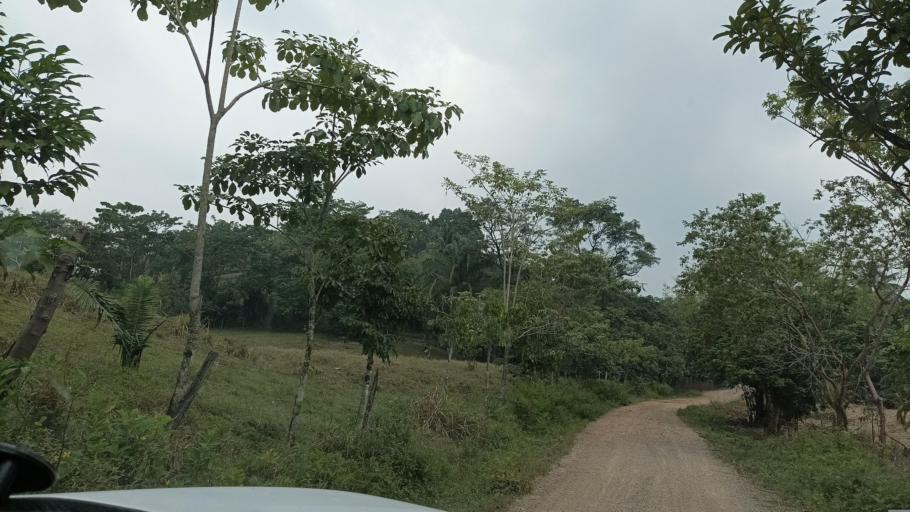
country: MX
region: Veracruz
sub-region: Moloacan
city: Cuichapa
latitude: 17.5751
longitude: -94.2280
